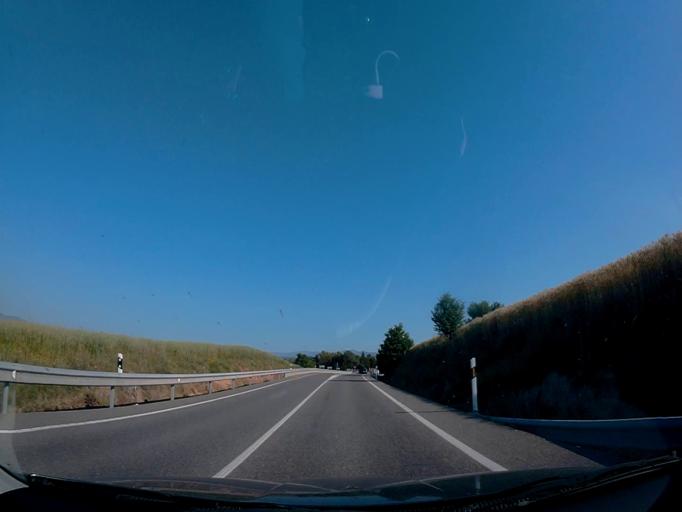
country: ES
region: Castille-La Mancha
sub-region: Province of Toledo
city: Hormigos
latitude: 40.1206
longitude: -4.4080
